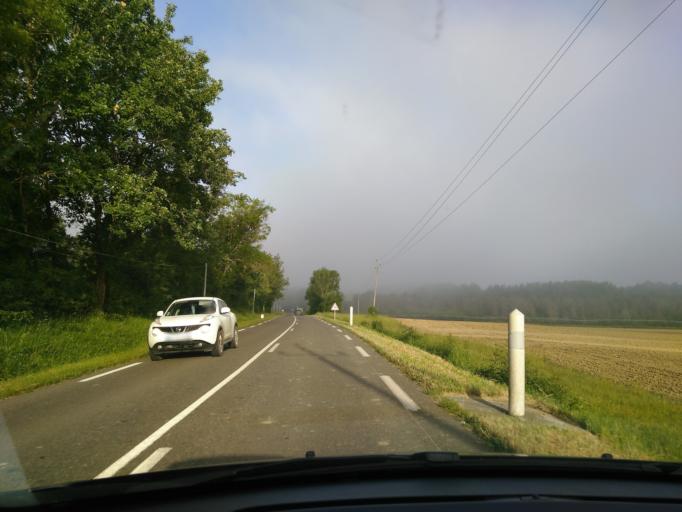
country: FR
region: Midi-Pyrenees
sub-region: Departement du Gers
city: Gondrin
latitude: 43.8784
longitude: 0.1835
